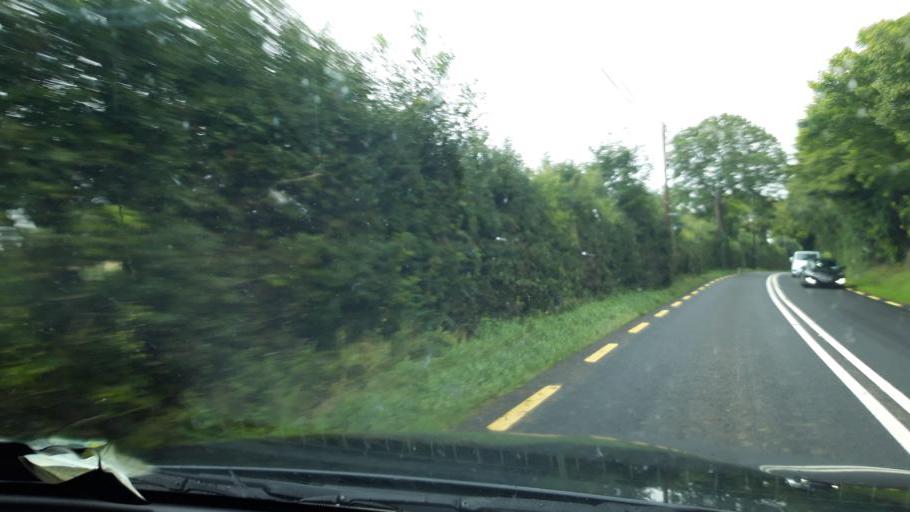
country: IE
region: Leinster
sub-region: Loch Garman
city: New Ross
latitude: 52.4286
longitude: -6.8252
